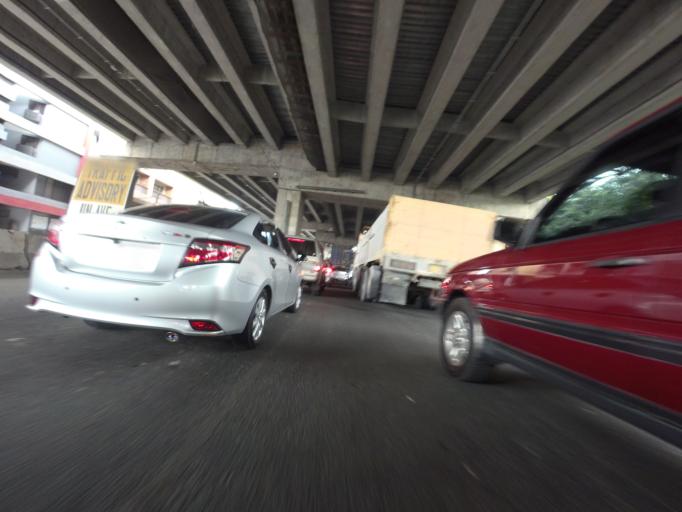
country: PH
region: Metro Manila
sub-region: City of Manila
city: Quiapo
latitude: 14.5792
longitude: 120.9988
